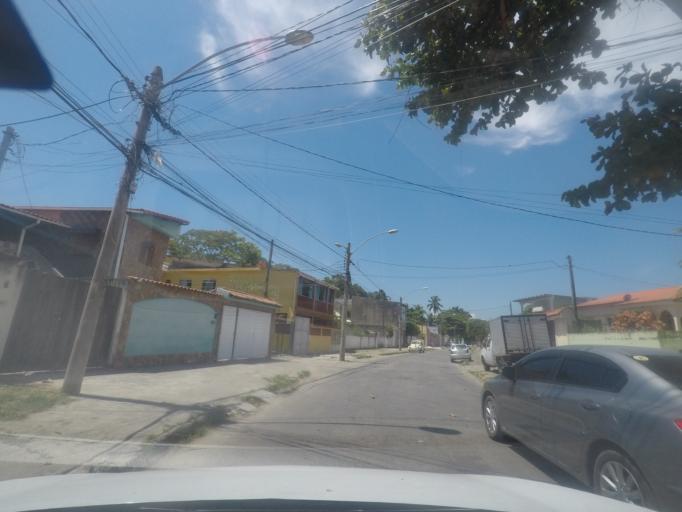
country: BR
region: Rio de Janeiro
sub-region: Itaguai
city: Itaguai
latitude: -23.0046
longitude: -43.6367
